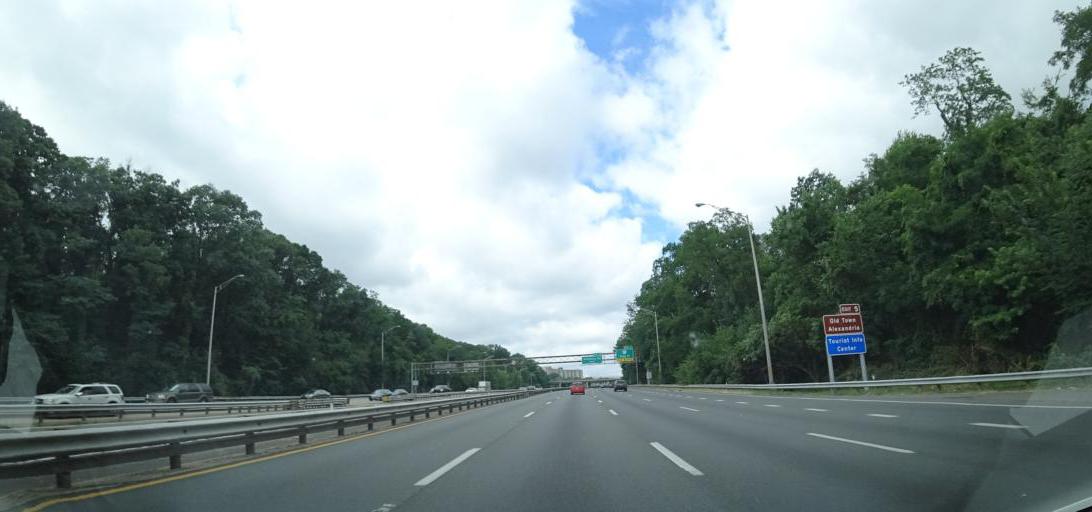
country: US
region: Virginia
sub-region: Fairfax County
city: Baileys Crossroads
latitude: 38.8372
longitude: -77.0905
